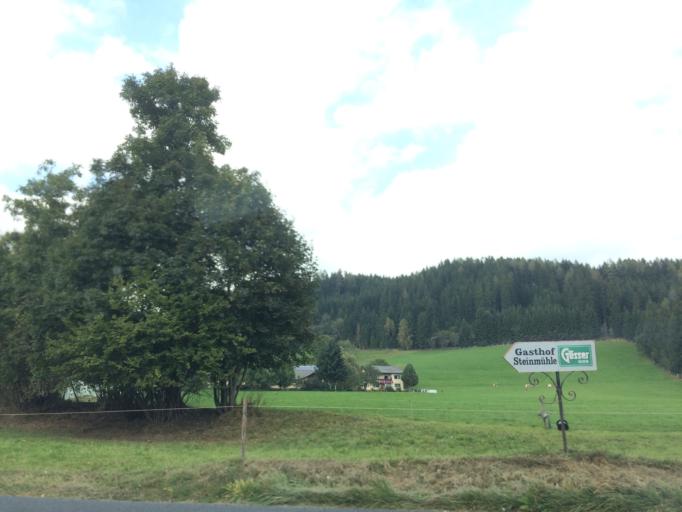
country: AT
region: Styria
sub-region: Politischer Bezirk Murtal
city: Seckau
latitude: 47.2763
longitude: 14.7628
